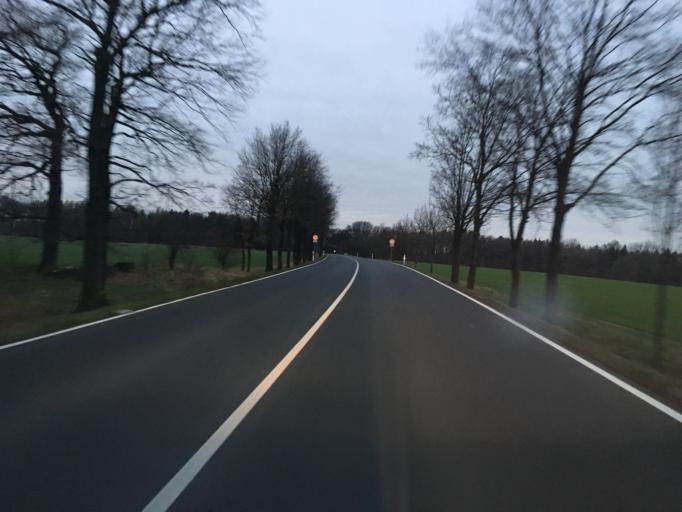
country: DE
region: Saxony
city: Dahlen
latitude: 51.3232
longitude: 13.0454
